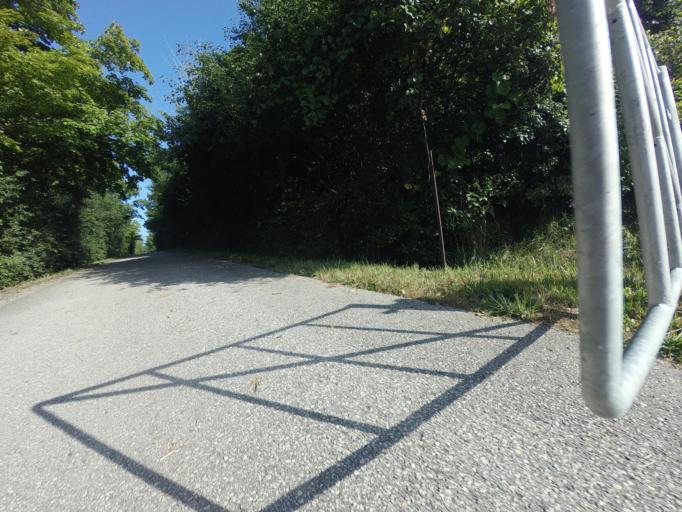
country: CA
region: Ontario
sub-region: Wellington County
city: Guelph
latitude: 43.6526
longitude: -80.4185
